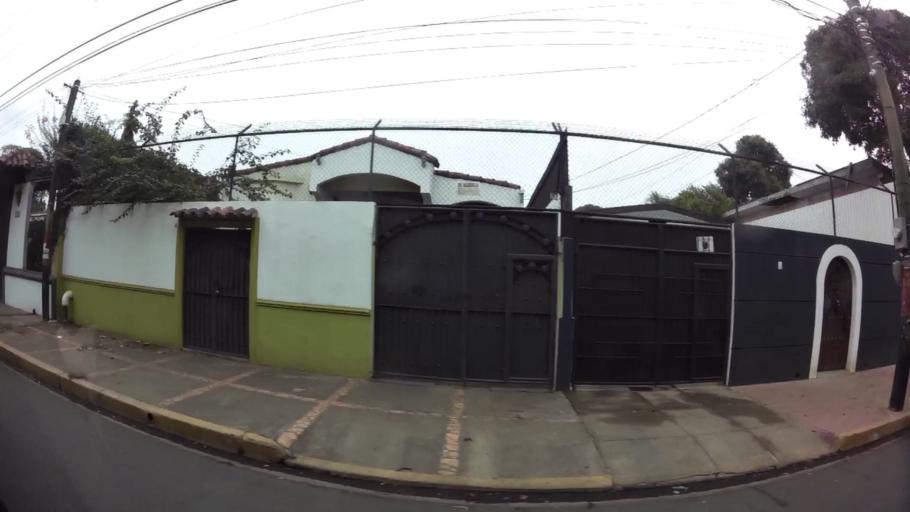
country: NI
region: Leon
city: Leon
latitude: 12.4512
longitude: -86.8707
